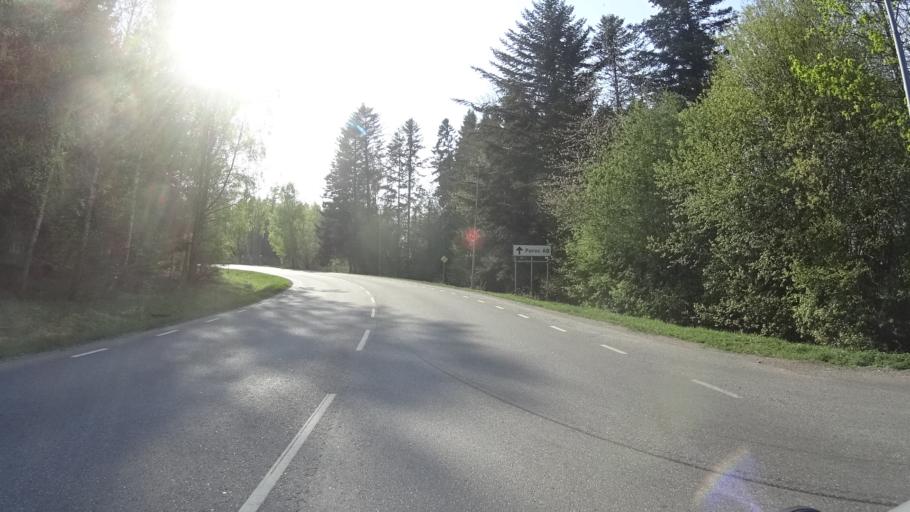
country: SE
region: Vaestra Goetaland
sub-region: Gotene Kommun
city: Goetene
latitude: 58.6323
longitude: 13.4378
